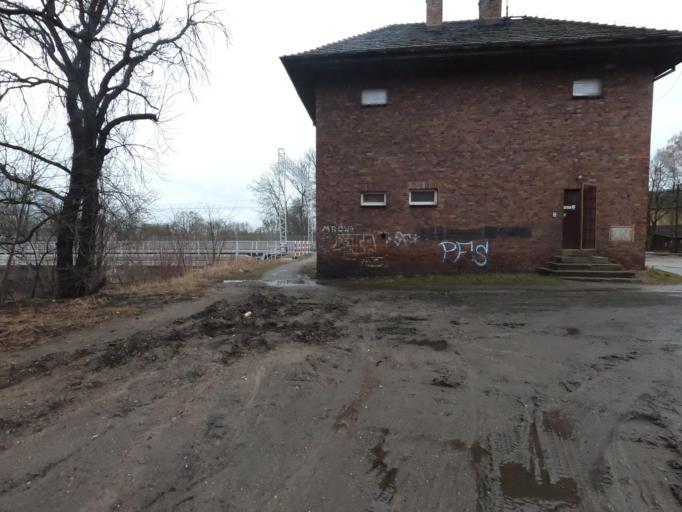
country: PL
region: Greater Poland Voivodeship
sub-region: Powiat pilski
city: Pila
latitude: 53.1443
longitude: 16.7541
